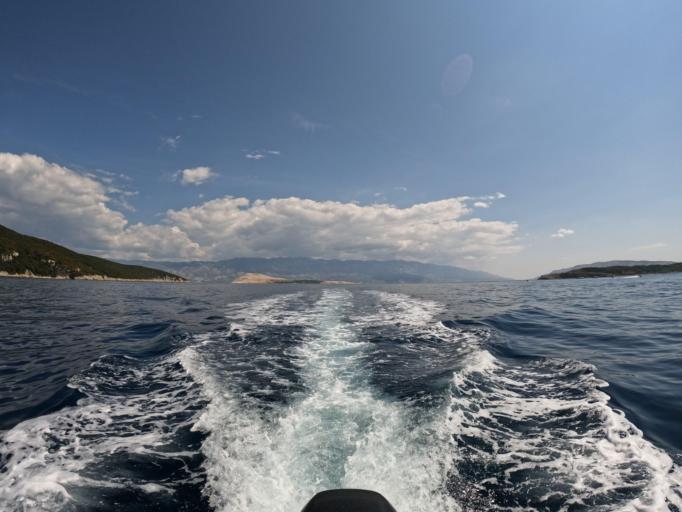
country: HR
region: Primorsko-Goranska
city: Lopar
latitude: 44.8537
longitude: 14.7526
